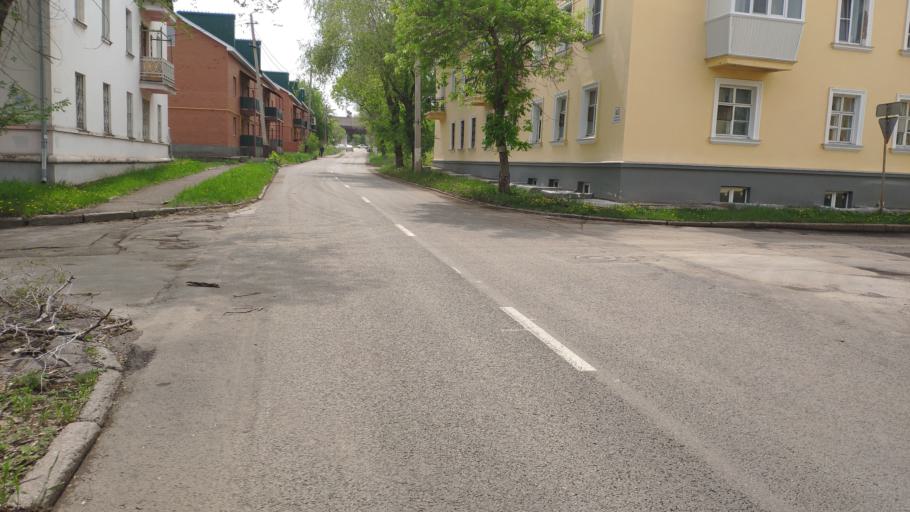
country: RU
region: Chelyabinsk
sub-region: Gorod Magnitogorsk
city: Magnitogorsk
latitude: 53.4196
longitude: 58.9553
